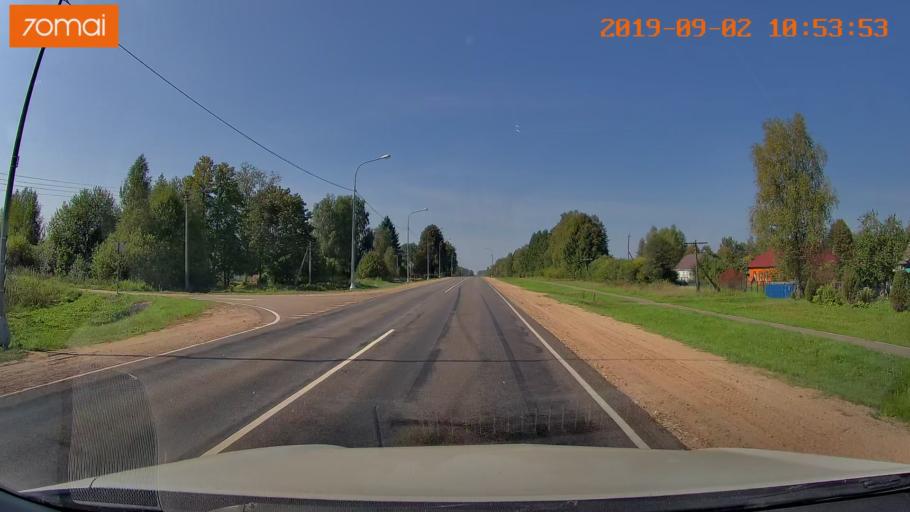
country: RU
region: Smolensk
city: Yekimovichi
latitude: 54.1962
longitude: 33.5679
